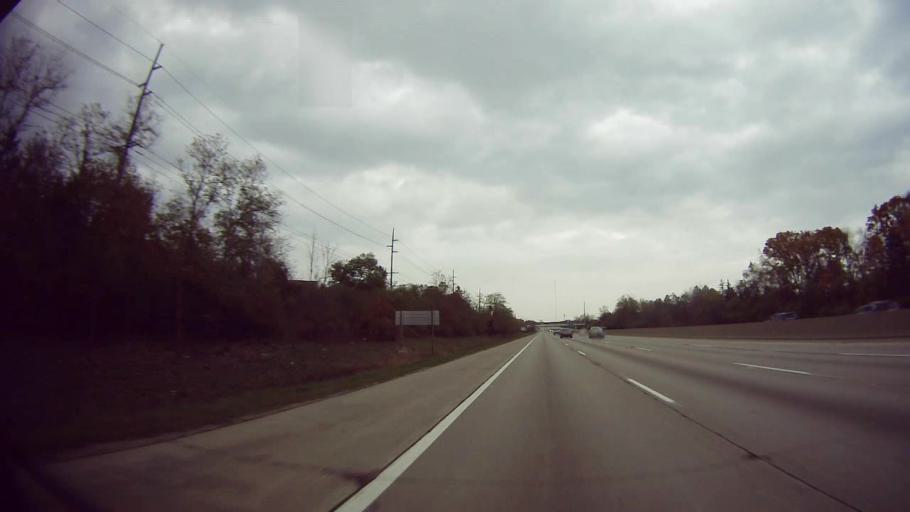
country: US
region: Michigan
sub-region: Oakland County
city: Farmington Hills
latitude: 42.4947
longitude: -83.3440
